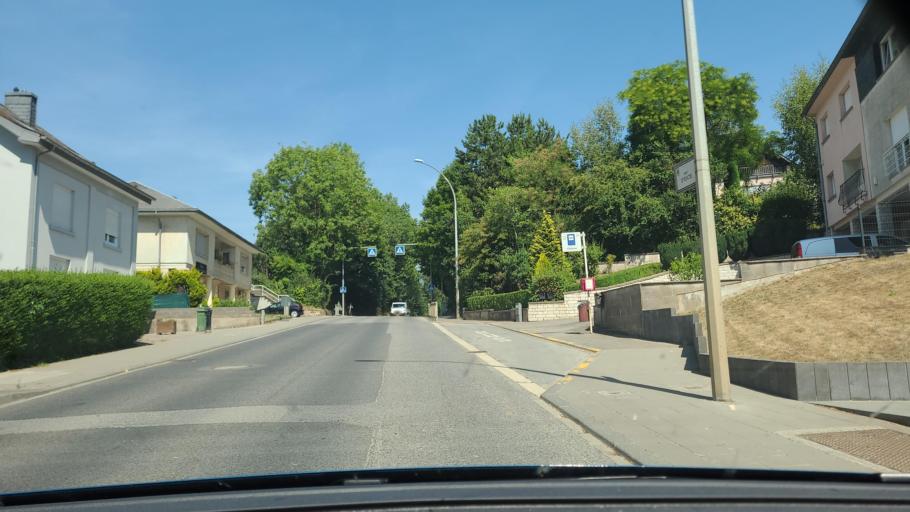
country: LU
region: Luxembourg
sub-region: Canton d'Esch-sur-Alzette
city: Sanem
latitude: 49.5441
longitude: 5.9314
